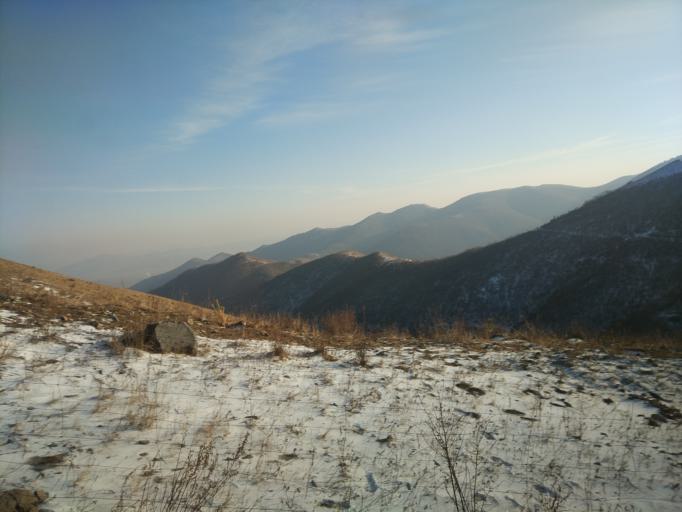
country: CN
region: Hebei
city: Xiwanzi
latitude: 40.8753
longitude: 115.4538
